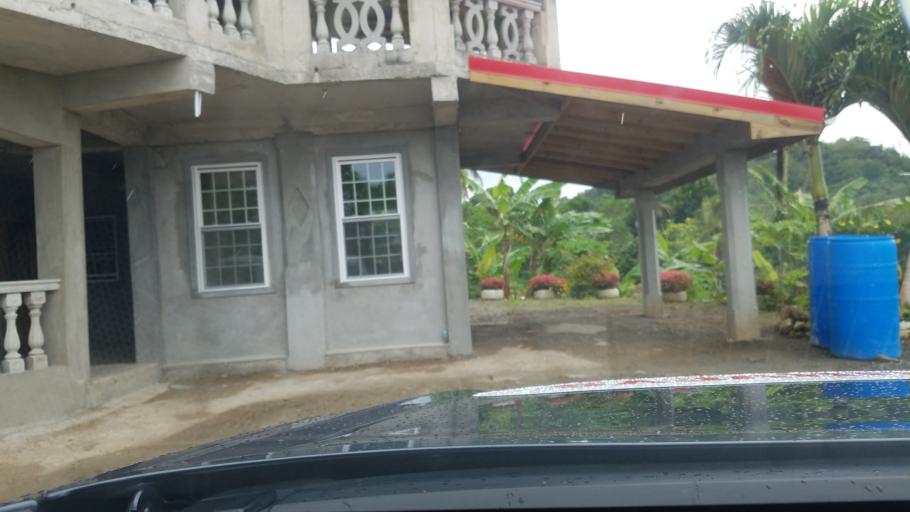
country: LC
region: Castries Quarter
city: Bisee
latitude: 13.9970
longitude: -60.9573
